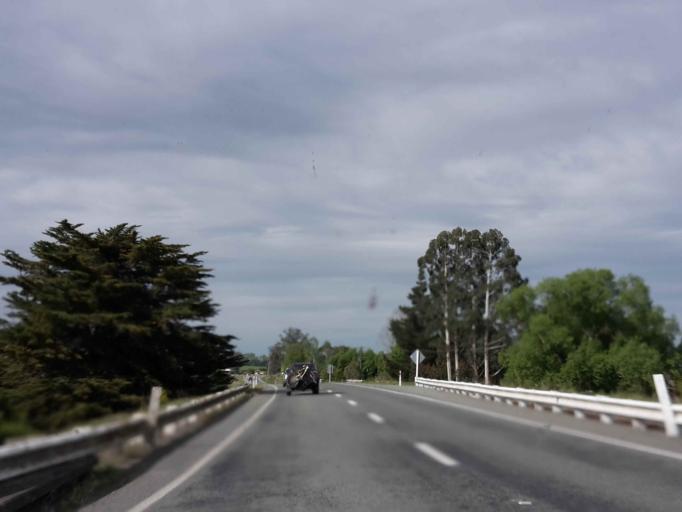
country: NZ
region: Canterbury
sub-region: Timaru District
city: Pleasant Point
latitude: -44.1163
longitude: 171.2100
